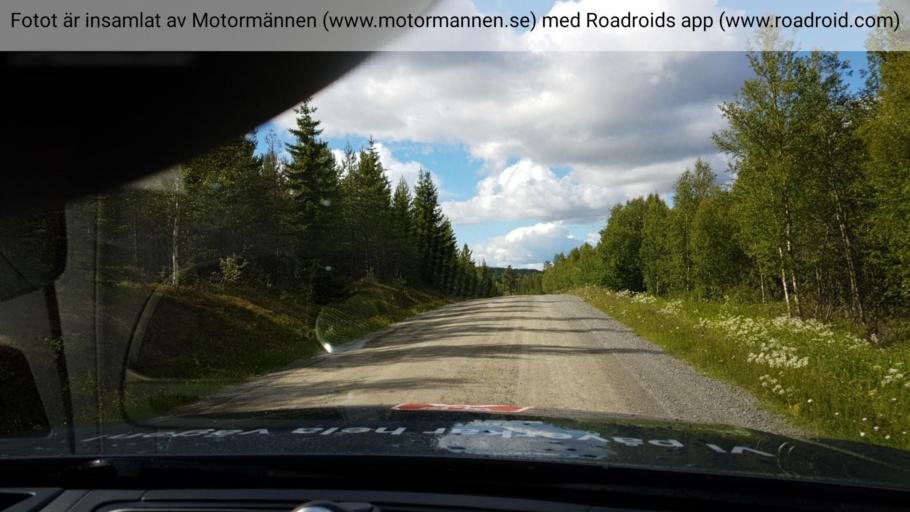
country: SE
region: Jaemtland
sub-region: Bergs Kommun
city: Hoverberg
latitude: 63.0254
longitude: 14.0784
